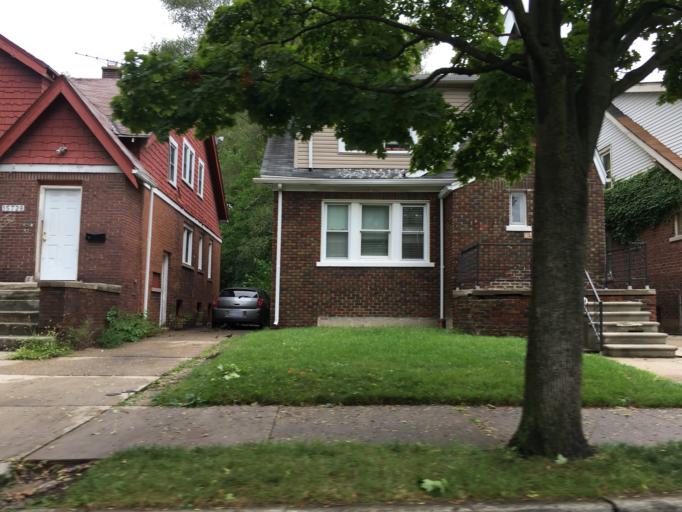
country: US
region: Michigan
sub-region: Oakland County
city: Oak Park
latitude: 42.4066
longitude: -83.1588
